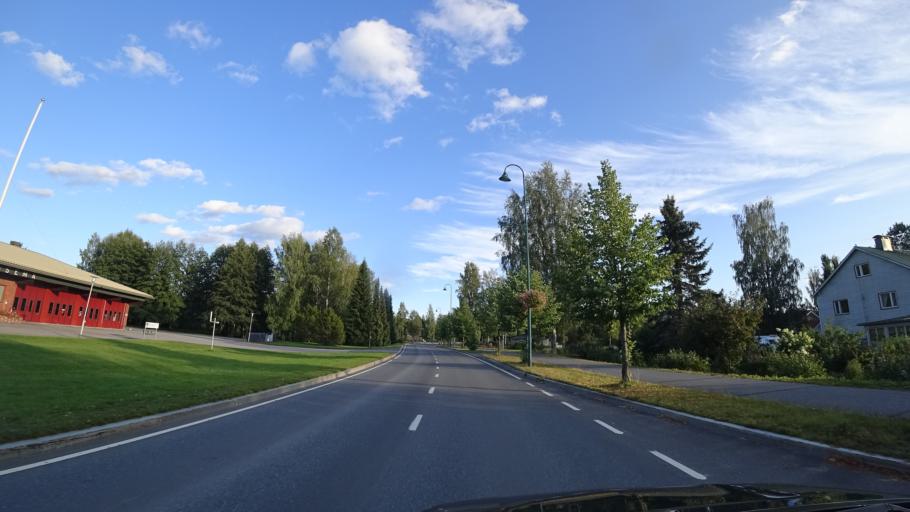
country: FI
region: Haeme
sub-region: Haemeenlinna
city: Lammi
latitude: 61.0745
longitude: 25.0116
